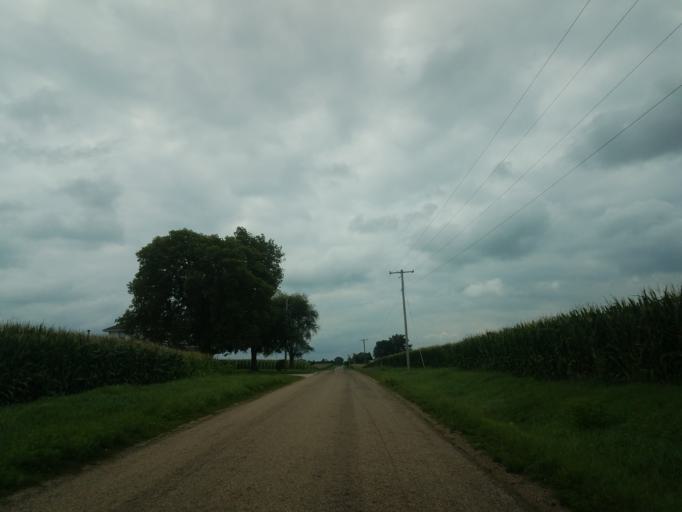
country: US
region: Illinois
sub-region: McLean County
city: Twin Grove
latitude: 40.4261
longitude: -89.0623
